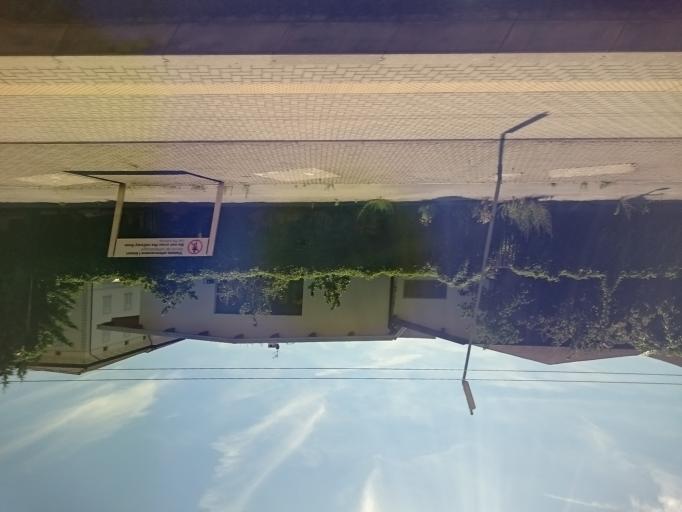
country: IT
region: Trentino-Alto Adige
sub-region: Provincia di Trento
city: Zambana
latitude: 46.1486
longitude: 11.0964
